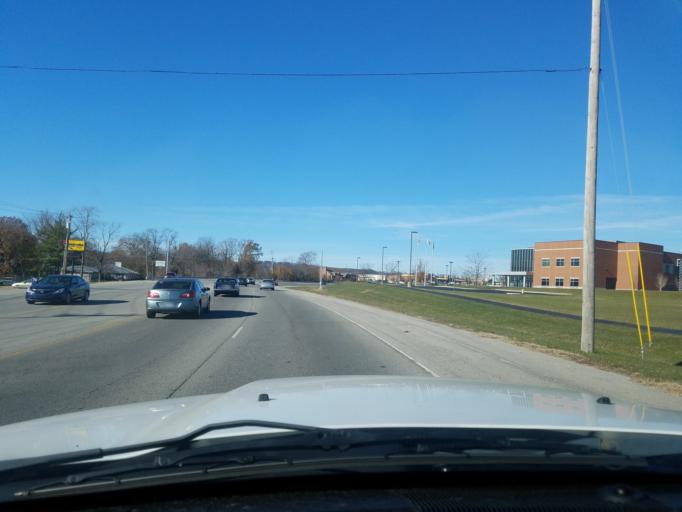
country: US
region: Indiana
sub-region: Clark County
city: Clarksville
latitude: 38.3372
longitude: -85.7989
